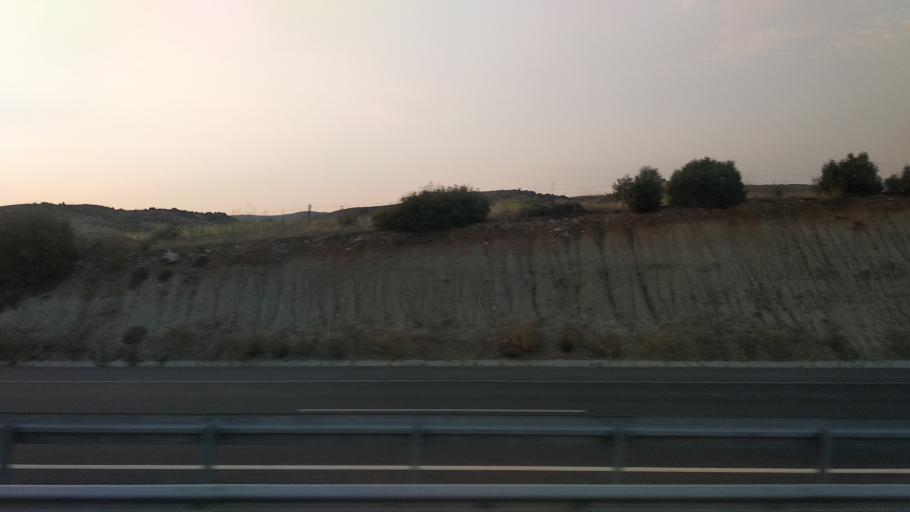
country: TR
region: Manisa
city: Selendi
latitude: 38.6260
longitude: 28.9310
